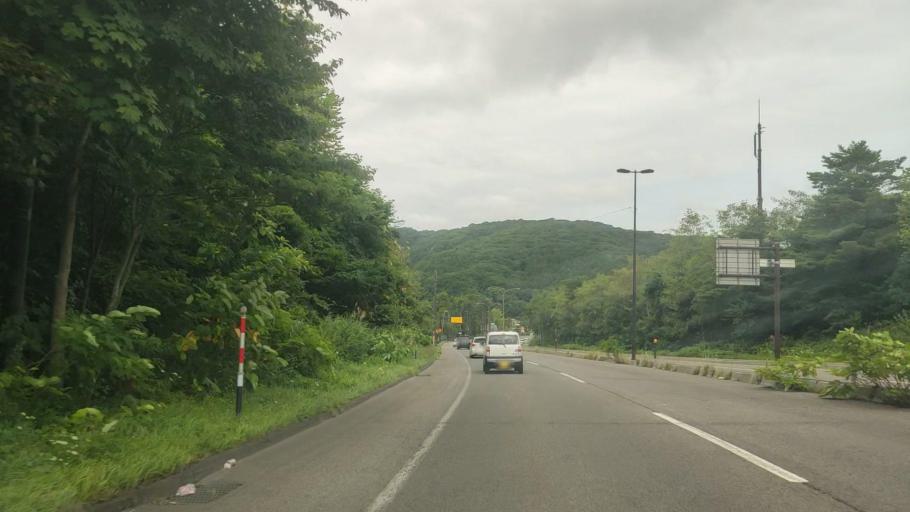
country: JP
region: Hokkaido
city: Nanae
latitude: 41.9583
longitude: 140.6494
